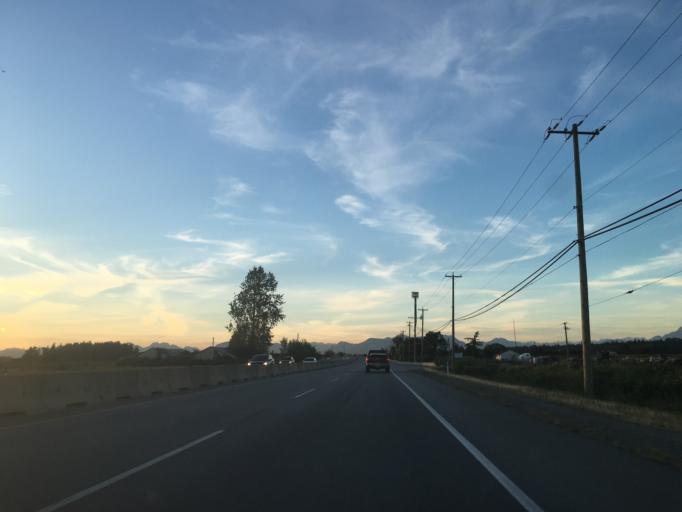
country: CA
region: British Columbia
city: Langley
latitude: 49.0827
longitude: -122.7353
